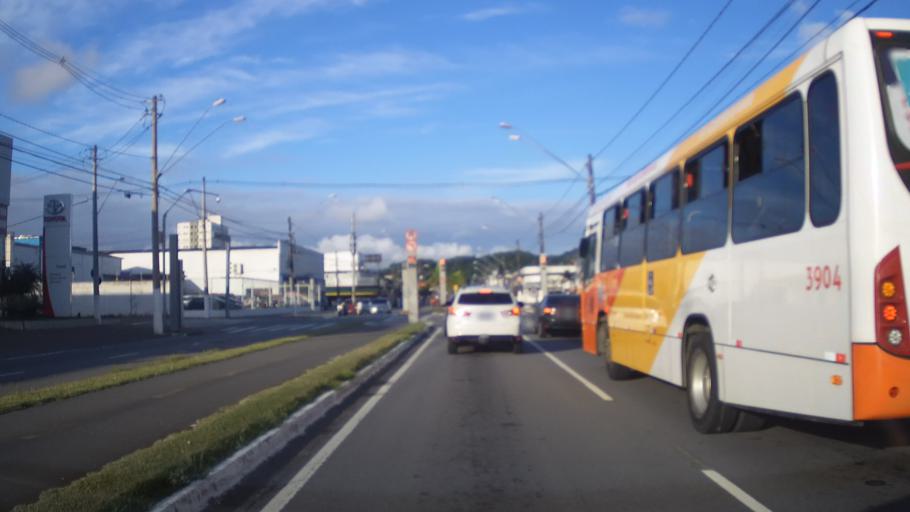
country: BR
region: Sao Paulo
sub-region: Praia Grande
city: Praia Grande
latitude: -24.0054
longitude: -46.4242
